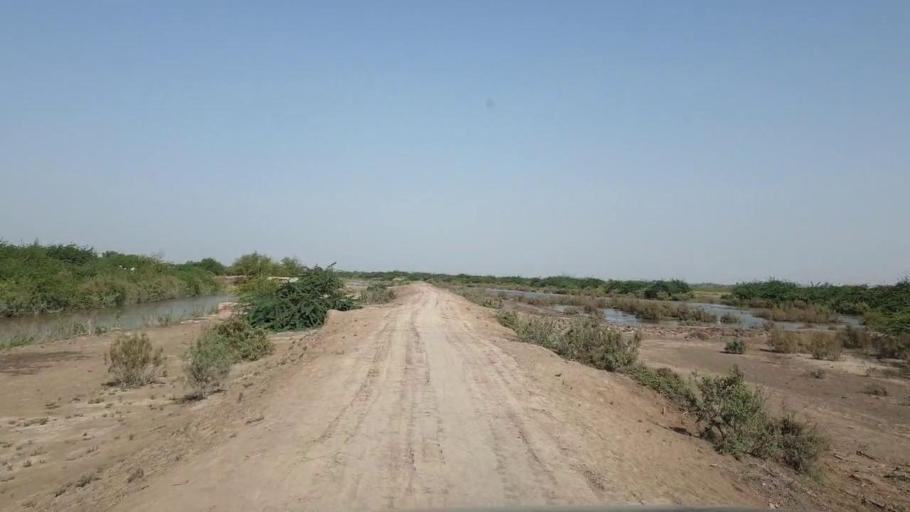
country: PK
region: Sindh
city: Tando Bago
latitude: 24.6553
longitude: 69.0703
